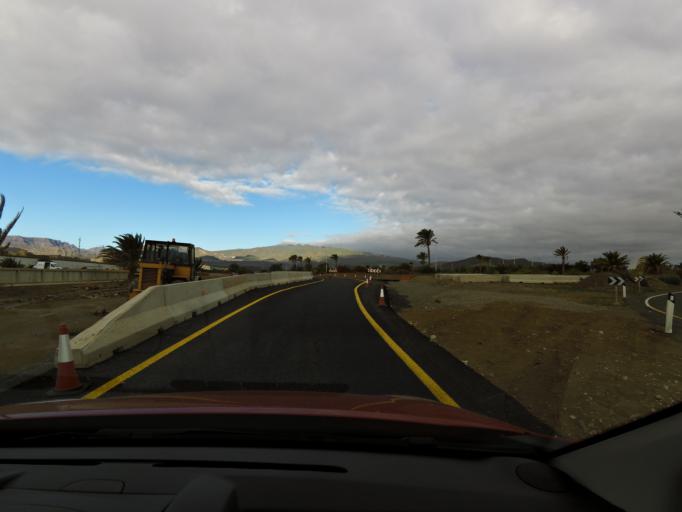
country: ES
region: Canary Islands
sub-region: Provincia de Las Palmas
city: Cruce de Arinaga
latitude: 27.8666
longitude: -15.4233
